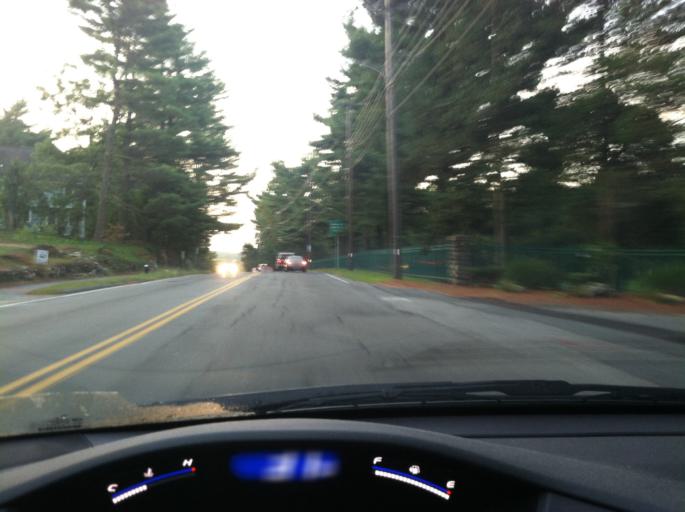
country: US
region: Massachusetts
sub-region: Middlesex County
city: Bedford
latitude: 42.4785
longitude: -71.2544
